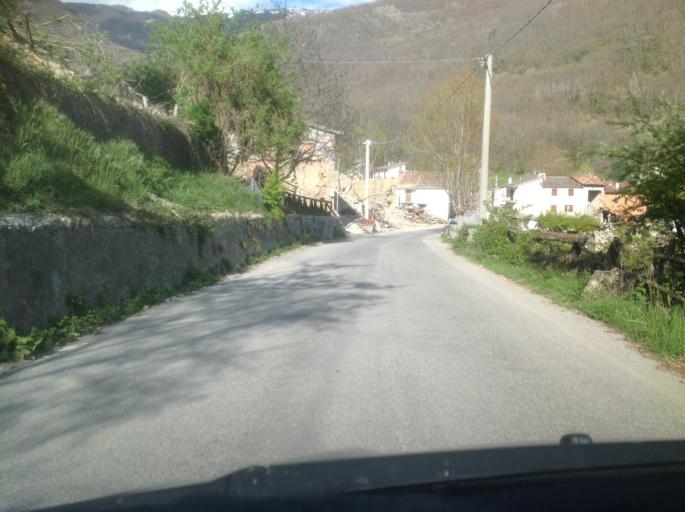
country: IT
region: Latium
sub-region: Provincia di Rieti
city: Amatrice
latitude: 42.6740
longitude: 13.2920
